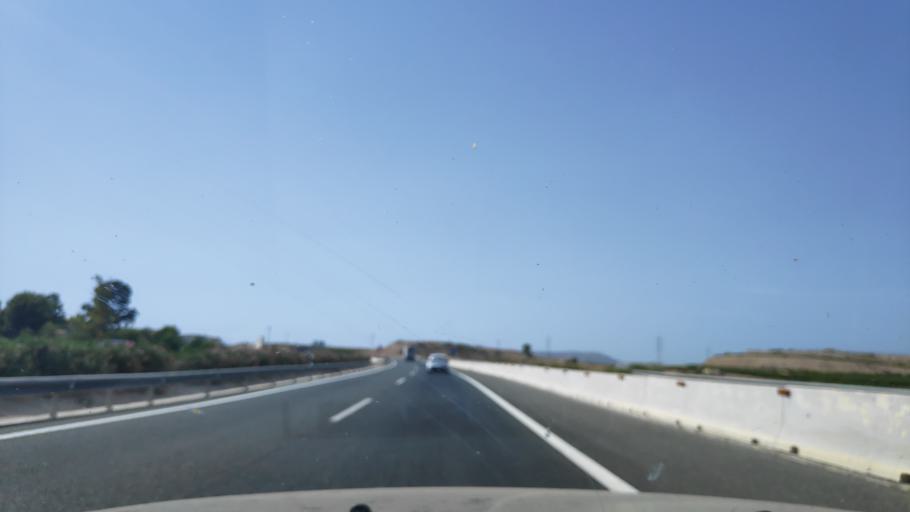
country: ES
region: Murcia
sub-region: Murcia
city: Blanca
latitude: 38.1932
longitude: -1.3314
